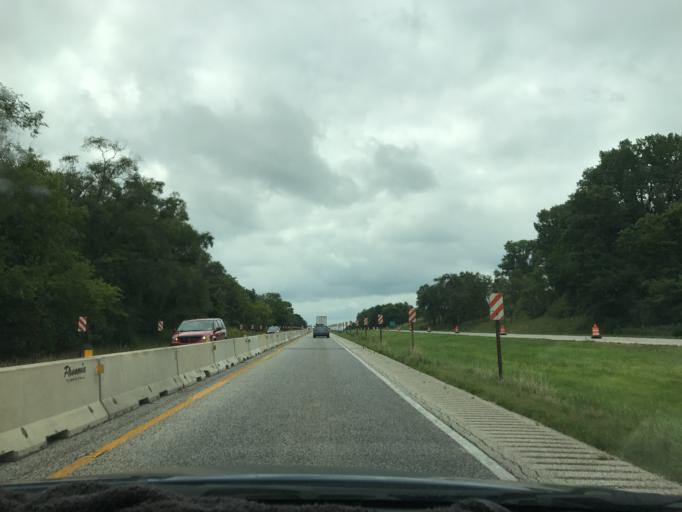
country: US
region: Illinois
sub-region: Henry County
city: Colona
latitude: 41.5002
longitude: -90.3386
